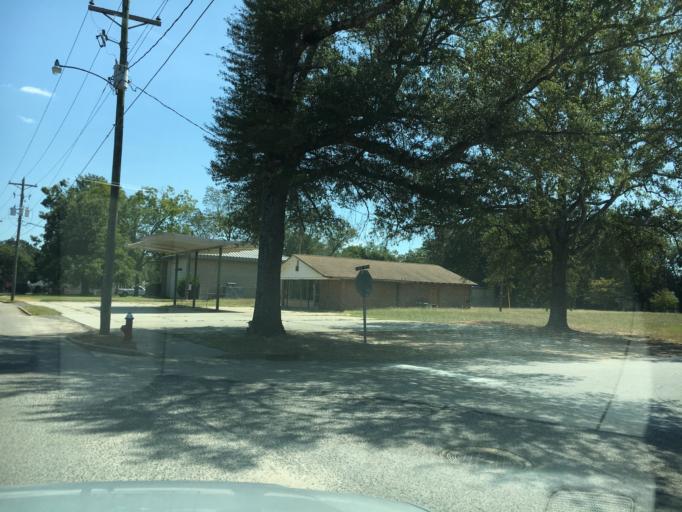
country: US
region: South Carolina
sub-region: Lexington County
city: Batesburg
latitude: 33.8455
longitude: -81.6583
